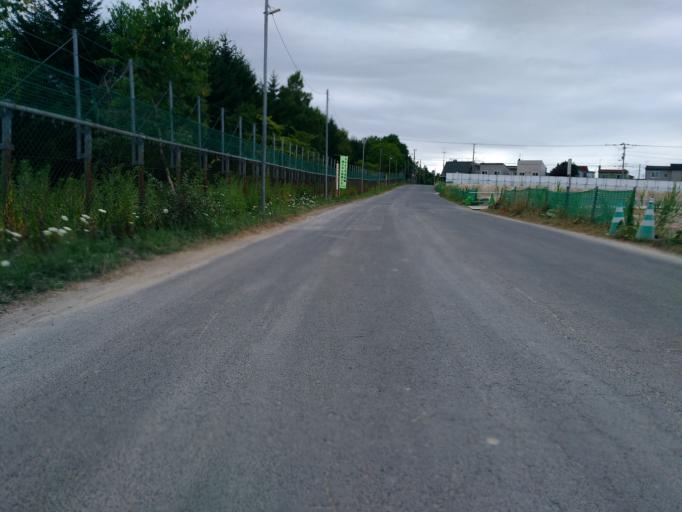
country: JP
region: Hokkaido
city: Ebetsu
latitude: 43.0813
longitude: 141.5285
